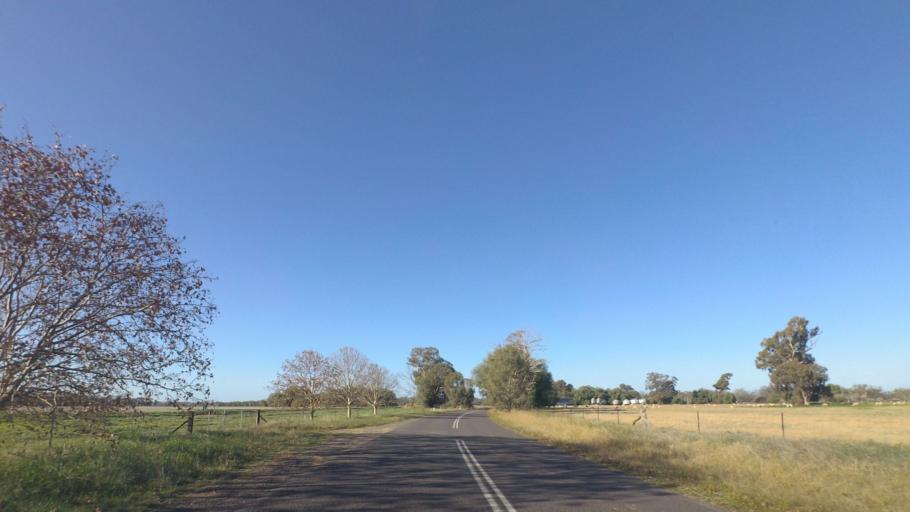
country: AU
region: Victoria
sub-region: Greater Bendigo
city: Epsom
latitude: -36.6468
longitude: 144.5324
